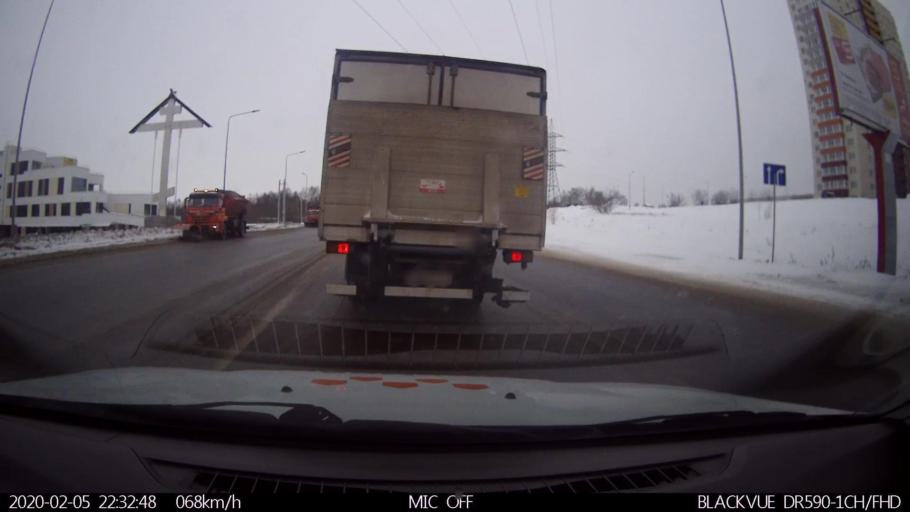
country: RU
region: Nizjnij Novgorod
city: Imeni Stepana Razina
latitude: 54.7372
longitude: 44.1968
